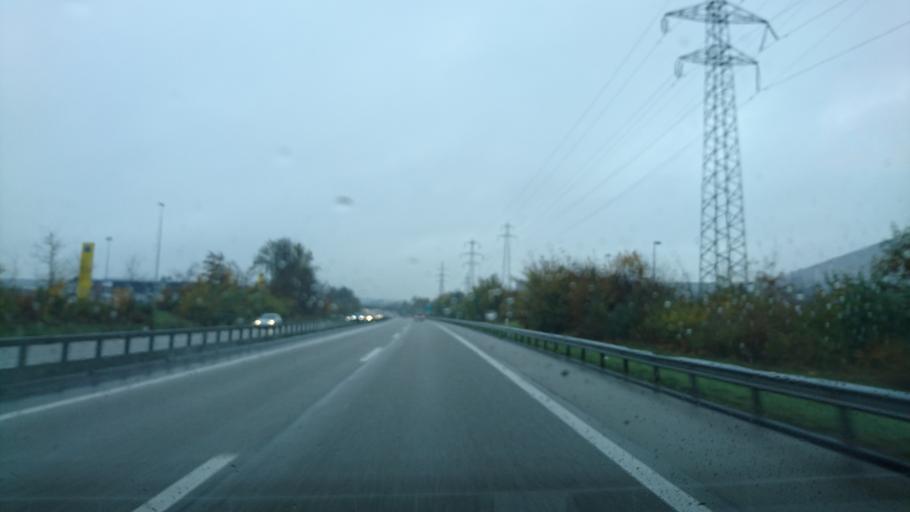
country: CH
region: Solothurn
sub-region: Bezirk Wasseramt
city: Derendingen
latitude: 47.1937
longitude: 7.5999
